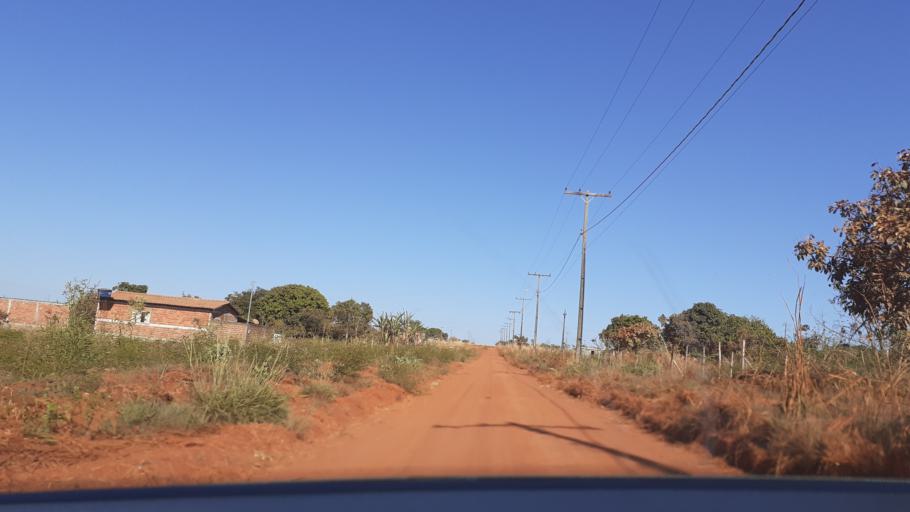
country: BR
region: Goias
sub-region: Aparecida De Goiania
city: Aparecida de Goiania
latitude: -16.8714
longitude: -49.2679
